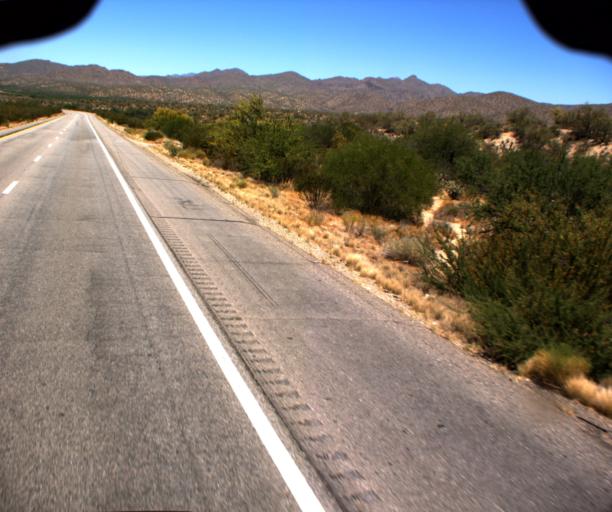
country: US
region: Arizona
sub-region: Yavapai County
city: Bagdad
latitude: 34.3638
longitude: -113.1750
